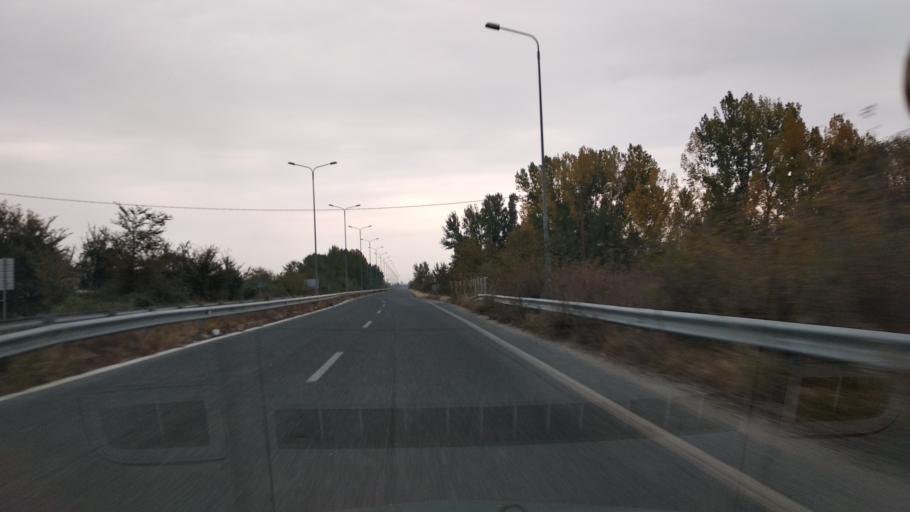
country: GR
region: Thessaly
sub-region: Trikala
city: Pyrgetos
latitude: 39.5418
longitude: 21.7357
